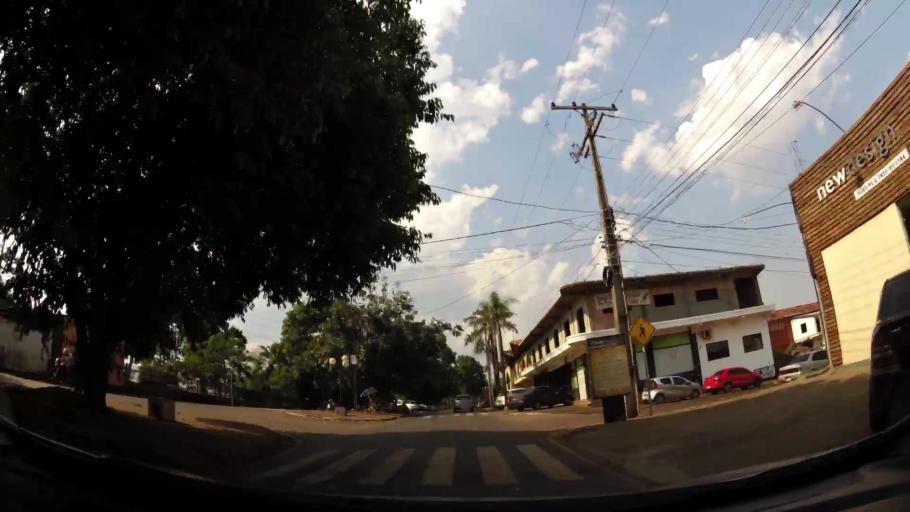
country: PY
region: Alto Parana
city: Ciudad del Este
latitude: -25.5034
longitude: -54.6283
